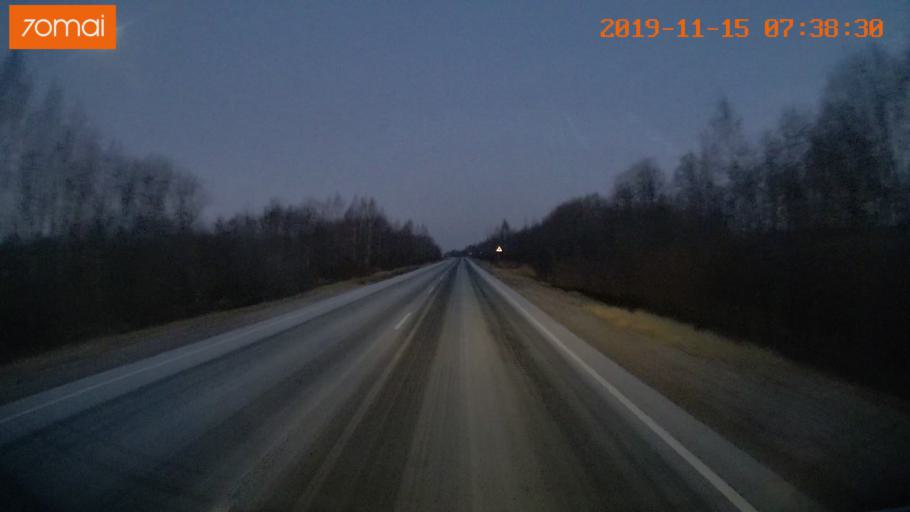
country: RU
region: Vologda
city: Sheksna
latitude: 58.7579
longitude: 38.4002
